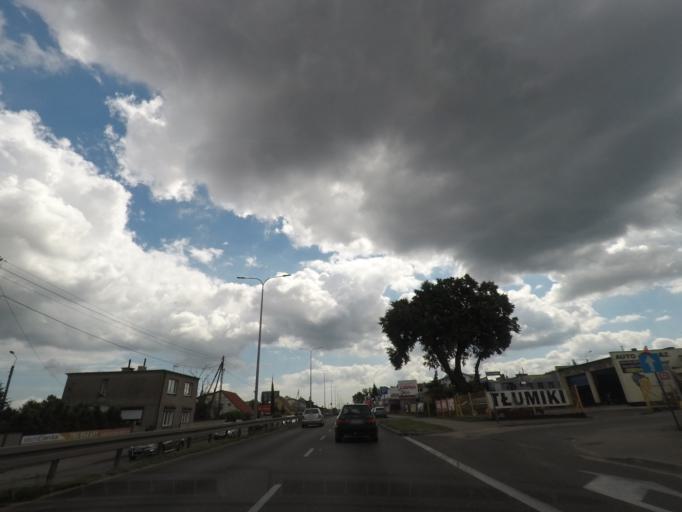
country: PL
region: Pomeranian Voivodeship
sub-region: Powiat wejherowski
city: Rumia
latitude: 54.5814
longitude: 18.3690
